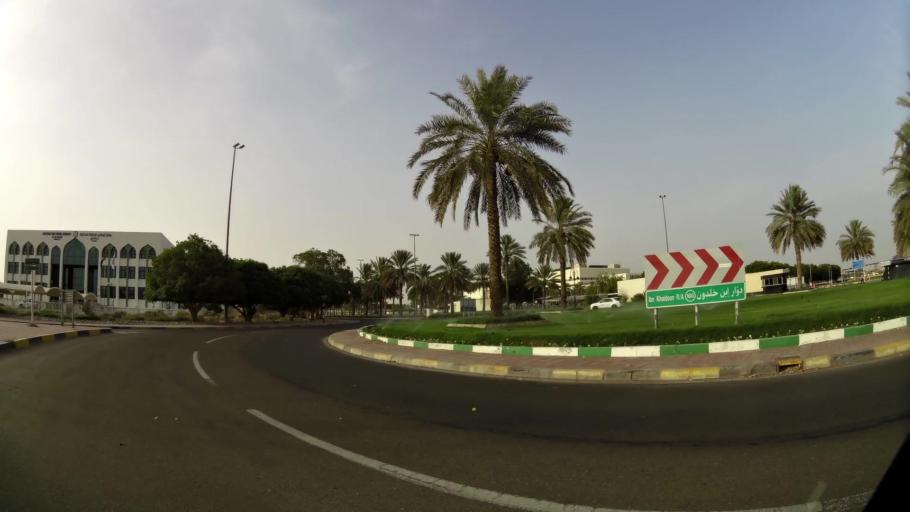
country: AE
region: Abu Dhabi
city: Al Ain
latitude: 24.2367
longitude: 55.7351
